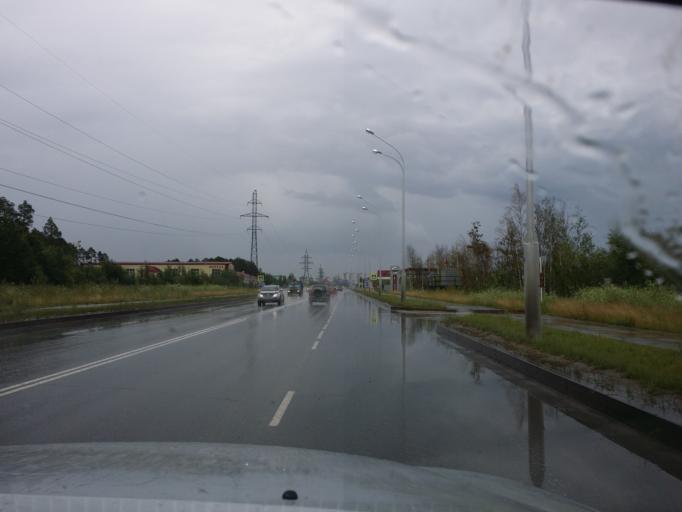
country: RU
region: Khanty-Mansiyskiy Avtonomnyy Okrug
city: Nizhnevartovsk
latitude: 60.9646
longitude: 76.5477
